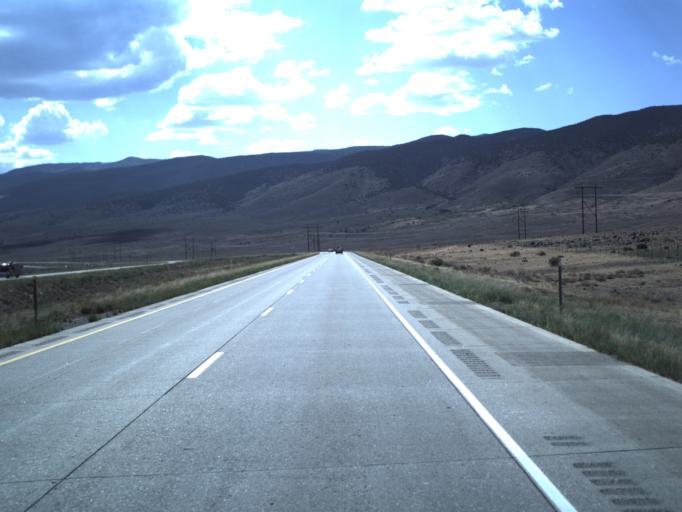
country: US
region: Utah
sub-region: Sevier County
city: Monroe
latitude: 38.6589
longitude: -112.1931
